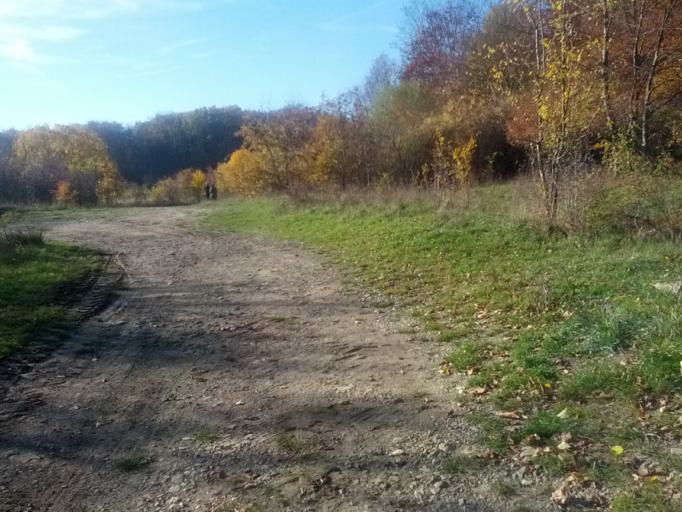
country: DE
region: Thuringia
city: Remstadt
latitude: 50.9570
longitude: 10.6586
